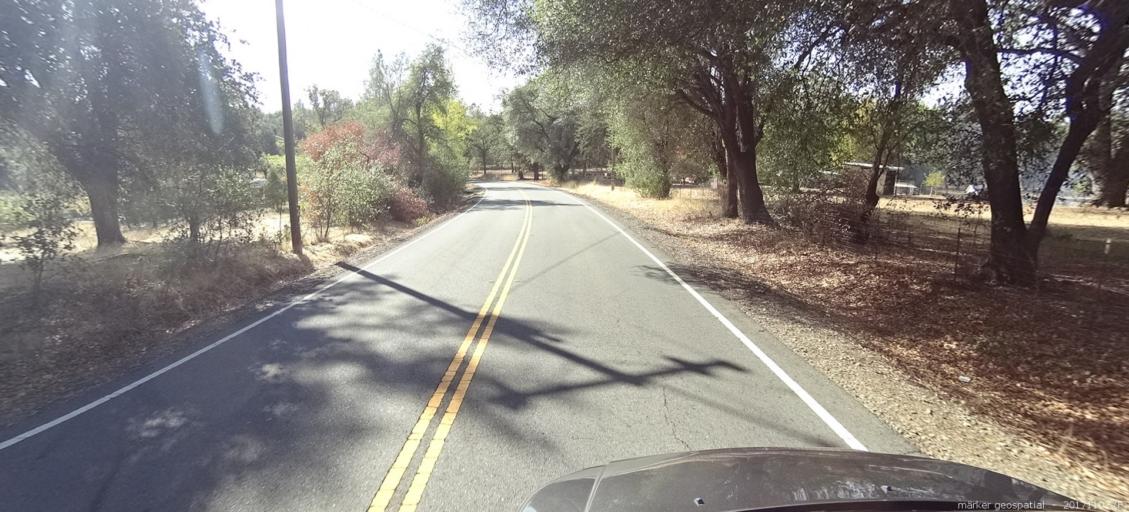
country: US
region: California
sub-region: Shasta County
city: Shasta
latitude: 40.4970
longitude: -122.5463
